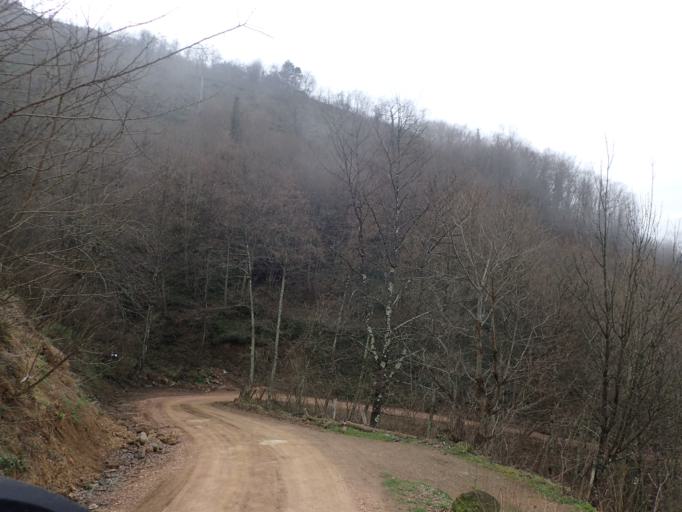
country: TR
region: Ordu
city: Camas
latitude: 40.8891
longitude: 37.5113
